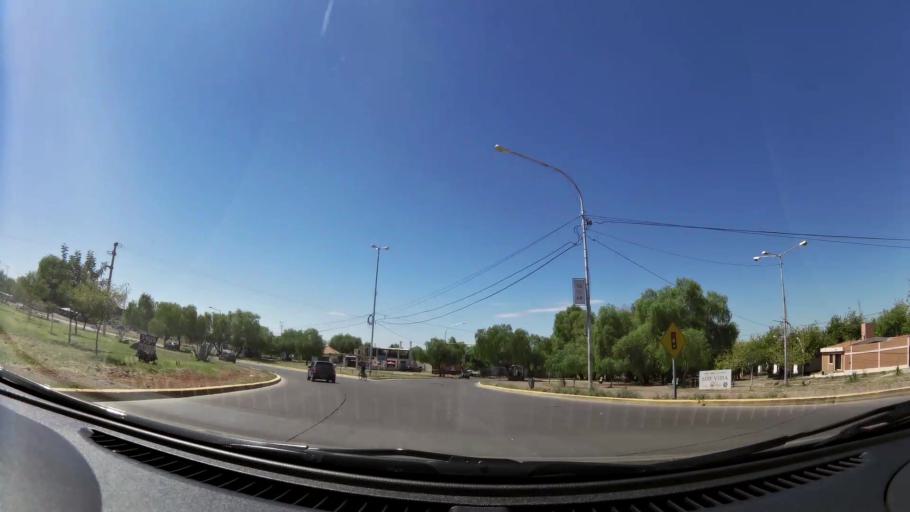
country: AR
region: Mendoza
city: Las Heras
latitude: -32.8530
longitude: -68.8591
